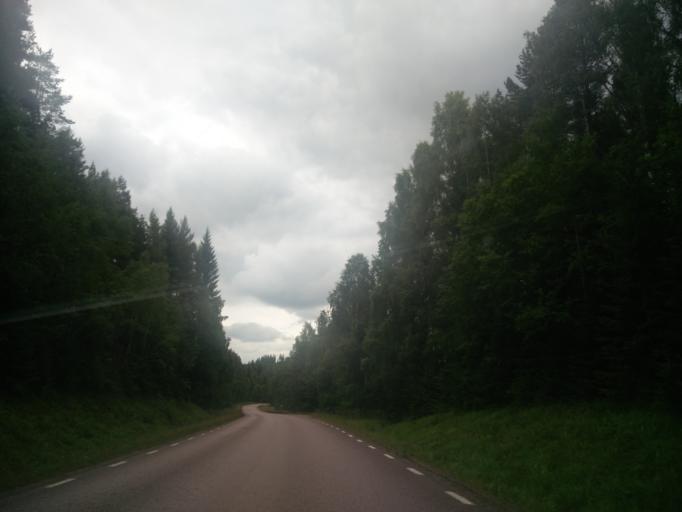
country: SE
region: Vaermland
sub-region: Arvika Kommun
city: Arvika
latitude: 59.9212
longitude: 12.6545
